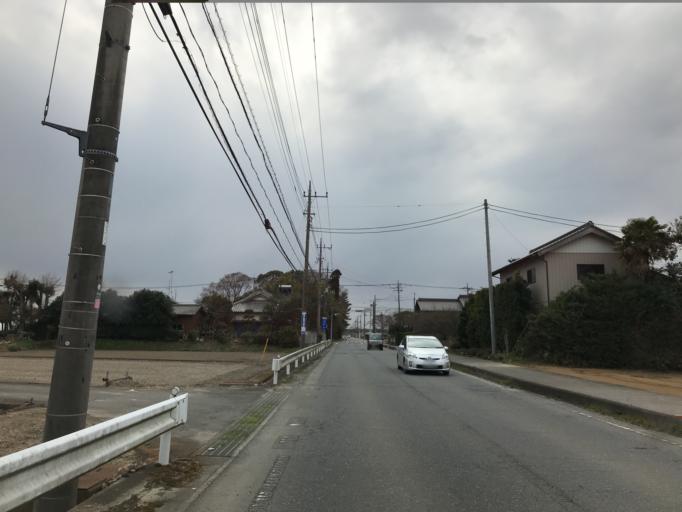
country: JP
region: Ibaraki
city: Moriya
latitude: 35.9649
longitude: 140.0385
